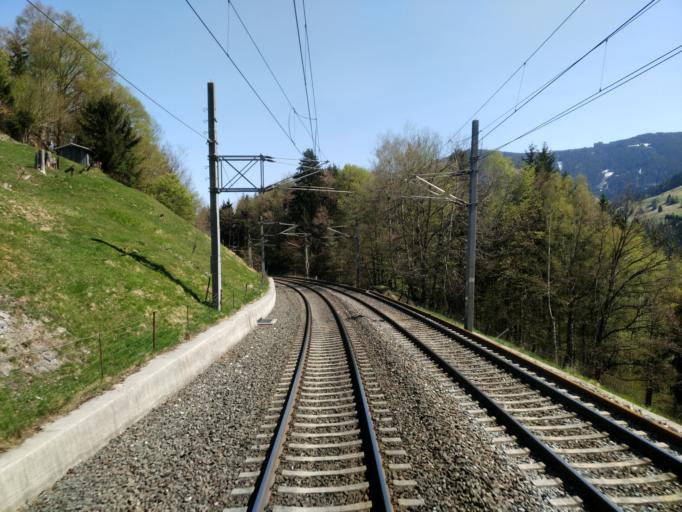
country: AT
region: Salzburg
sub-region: Politischer Bezirk Zell am See
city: Leogang
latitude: 47.4414
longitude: 12.7487
